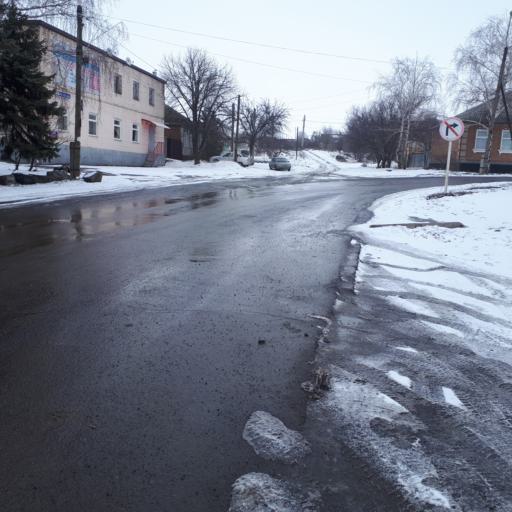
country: RU
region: Rostov
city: Krasnyy Sulin
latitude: 47.9009
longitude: 40.0538
